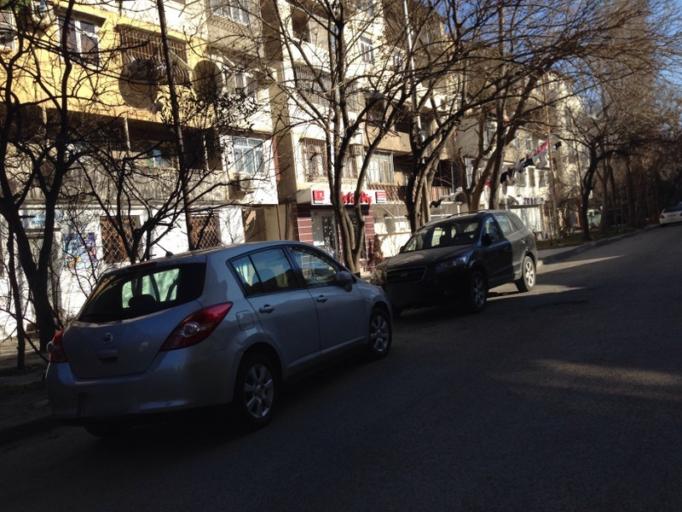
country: AZ
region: Baki
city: Baku
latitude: 40.4024
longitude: 49.8657
